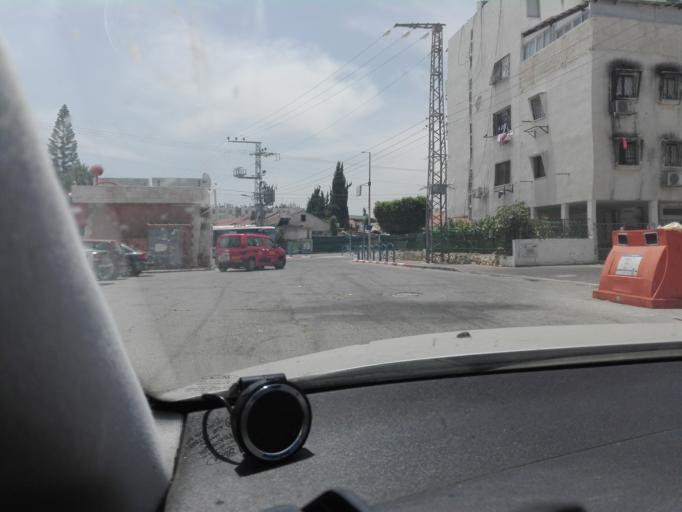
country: IL
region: Central District
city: Bene 'Ayish
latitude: 31.7363
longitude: 34.7398
